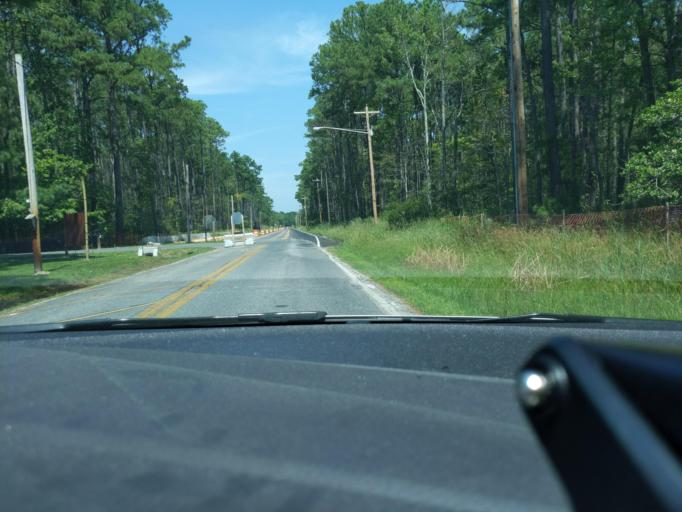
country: US
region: Virginia
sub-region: Northumberland County
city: Heathsville
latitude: 38.0645
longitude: -76.3356
